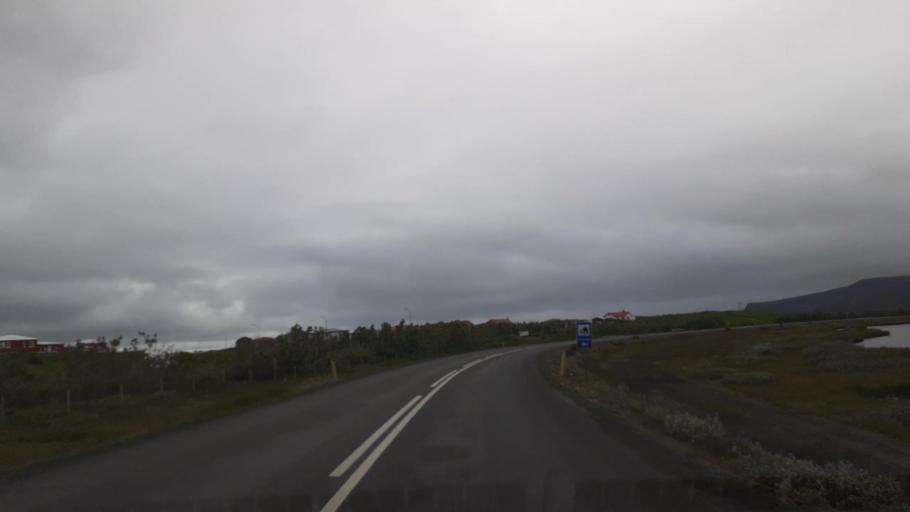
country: IS
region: Northeast
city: Husavik
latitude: 66.3002
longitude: -16.4386
